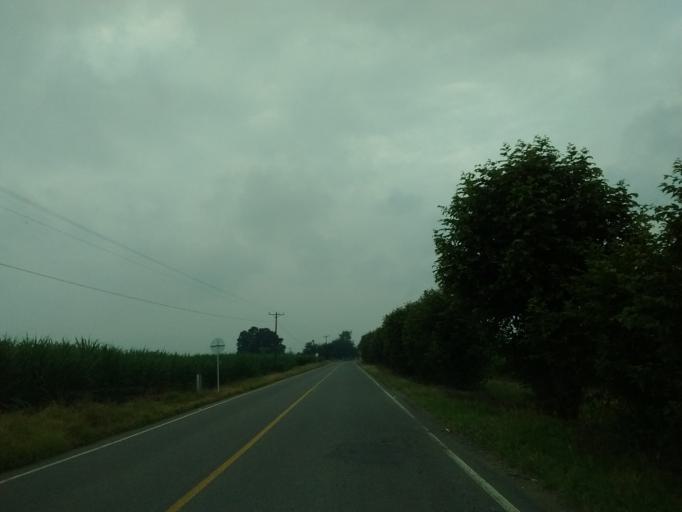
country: CO
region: Cauca
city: Puerto Tejada
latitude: 3.2229
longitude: -76.3827
